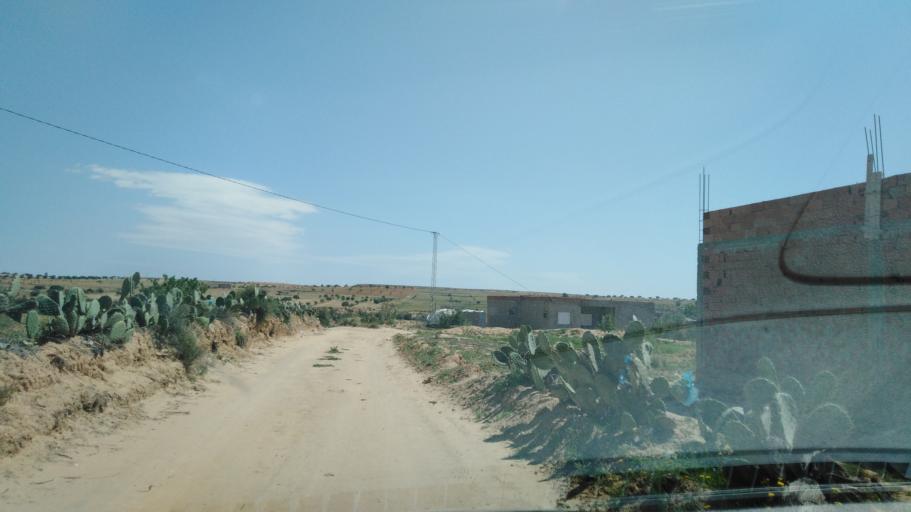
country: TN
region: Safaqis
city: Sfax
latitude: 34.7791
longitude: 10.5253
